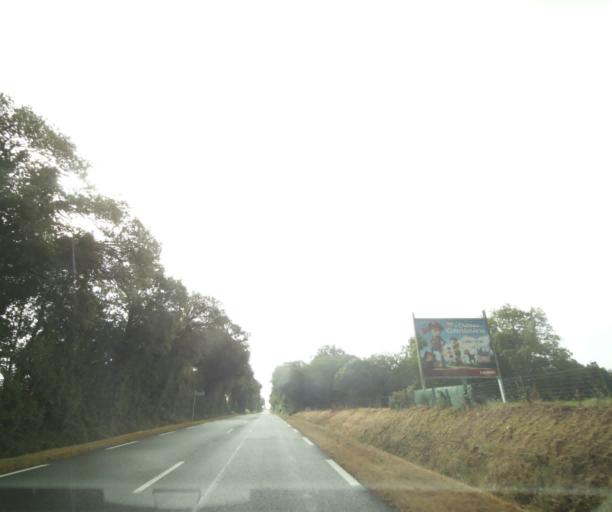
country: FR
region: Pays de la Loire
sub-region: Departement de la Vendee
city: Avrille
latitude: 46.4741
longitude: -1.5063
